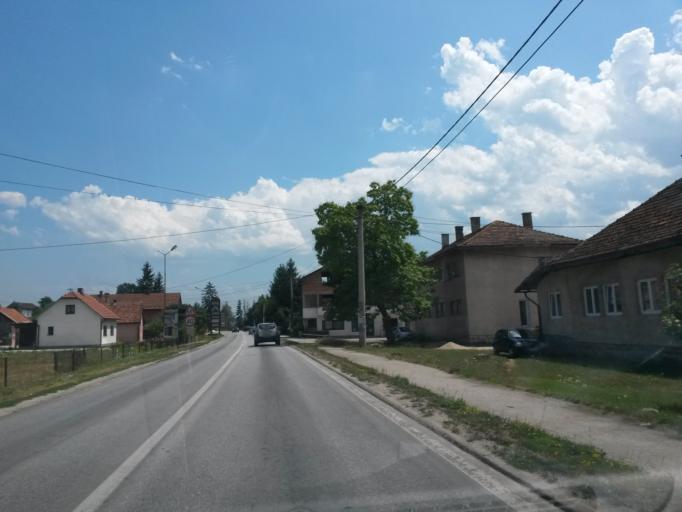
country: BA
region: Federation of Bosnia and Herzegovina
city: Vitez
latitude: 44.1912
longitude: 17.7352
